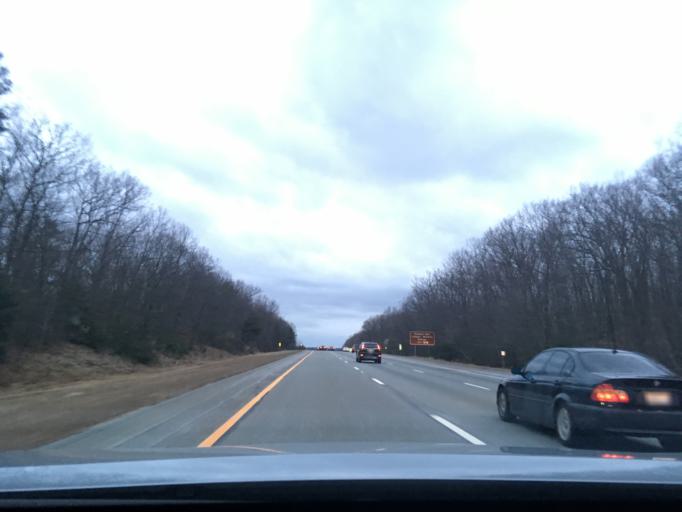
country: US
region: Rhode Island
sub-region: Providence County
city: Greenville
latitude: 41.8860
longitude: -71.5198
